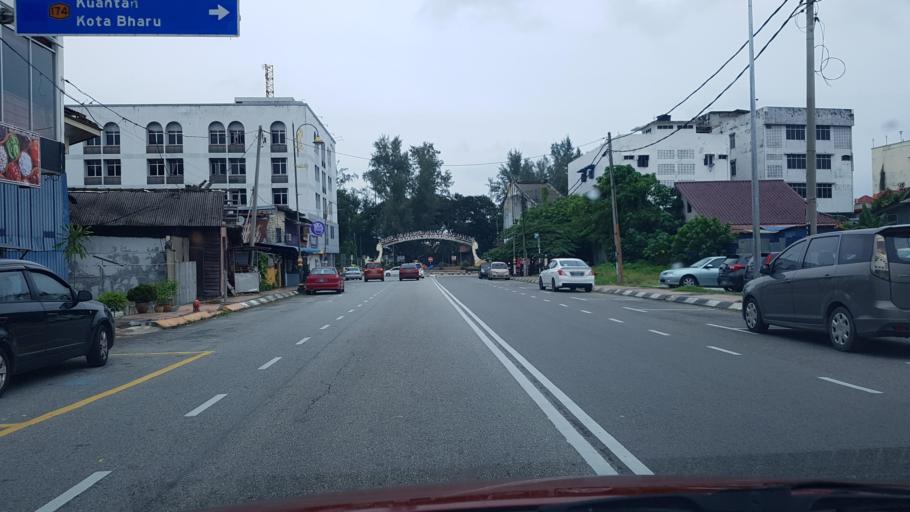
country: MY
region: Terengganu
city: Kuala Terengganu
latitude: 5.3360
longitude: 103.1392
